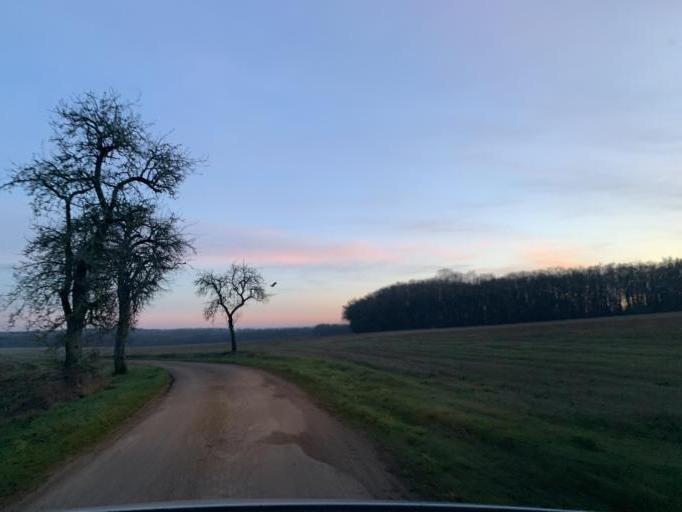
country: FR
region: Bourgogne
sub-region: Departement de l'Yonne
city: Fontenailles
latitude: 47.5612
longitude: 3.3473
